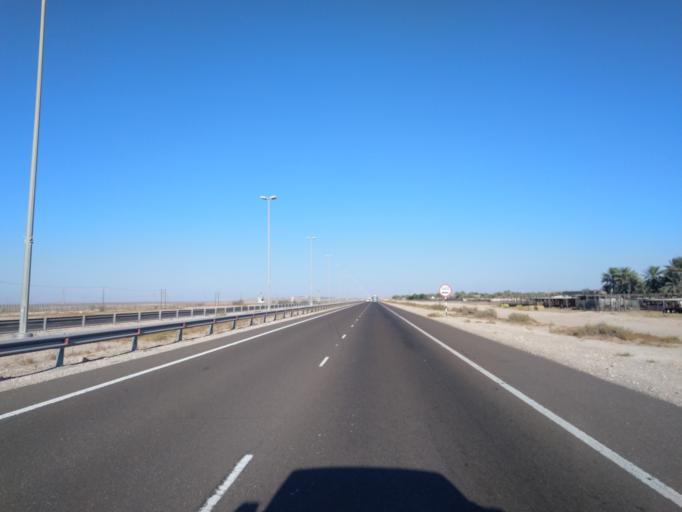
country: OM
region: Al Buraimi
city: Al Buraymi
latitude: 24.4888
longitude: 55.4006
